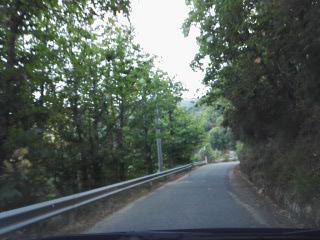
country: IT
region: Calabria
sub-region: Provincia di Vibo-Valentia
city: Nardodipace
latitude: 38.4413
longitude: 16.3403
